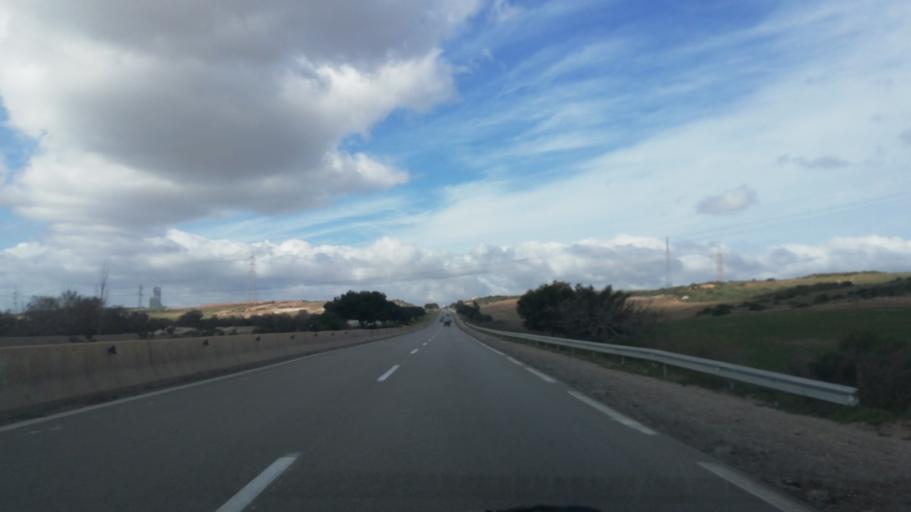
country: DZ
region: Oran
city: Ain el Bya
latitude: 35.7696
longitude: -0.2365
